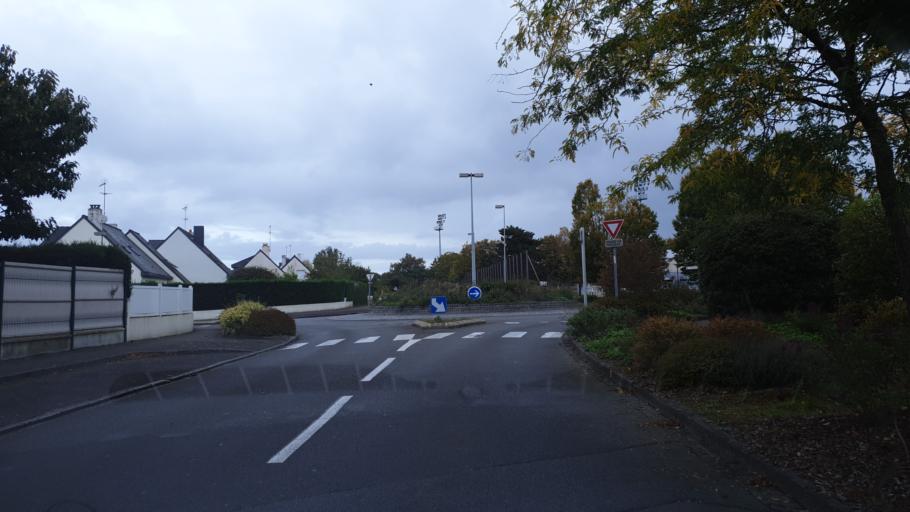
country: FR
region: Brittany
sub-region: Departement d'Ille-et-Vilaine
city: Chartres-de-Bretagne
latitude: 48.0447
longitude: -1.7059
